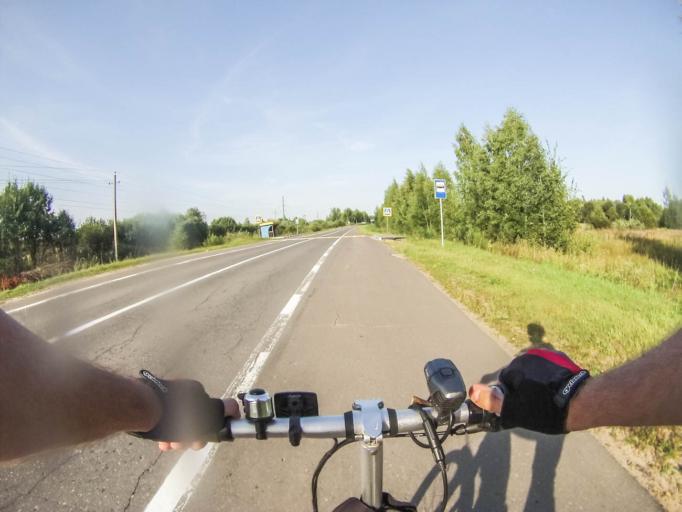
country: RU
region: Jaroslavl
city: Myshkin
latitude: 57.7042
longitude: 38.3568
